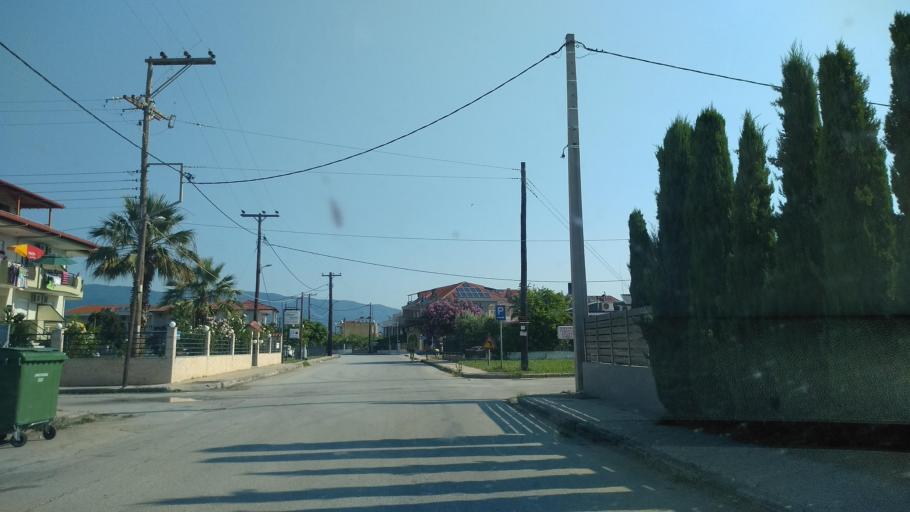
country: GR
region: Central Macedonia
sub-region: Nomos Thessalonikis
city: Stavros
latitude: 40.6696
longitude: 23.6917
